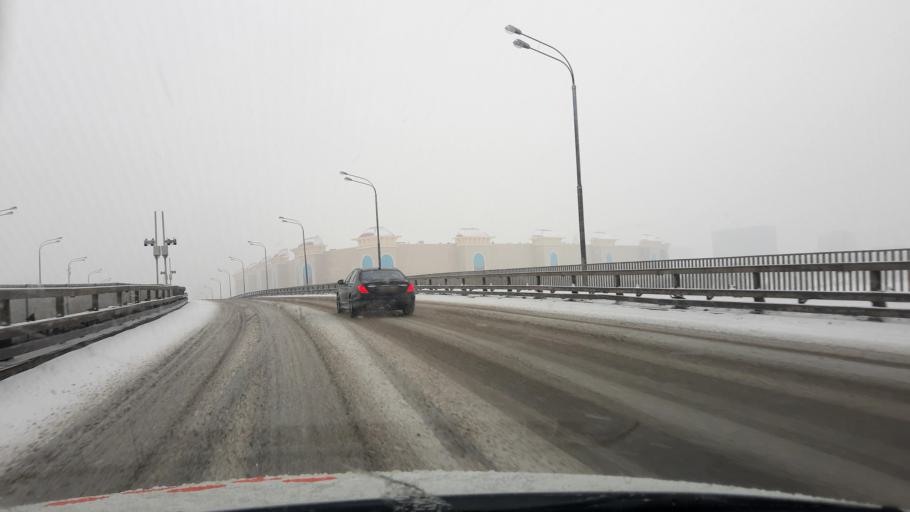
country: RU
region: Moskovskaya
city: Kozhukhovo
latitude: 55.6984
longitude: 37.6853
